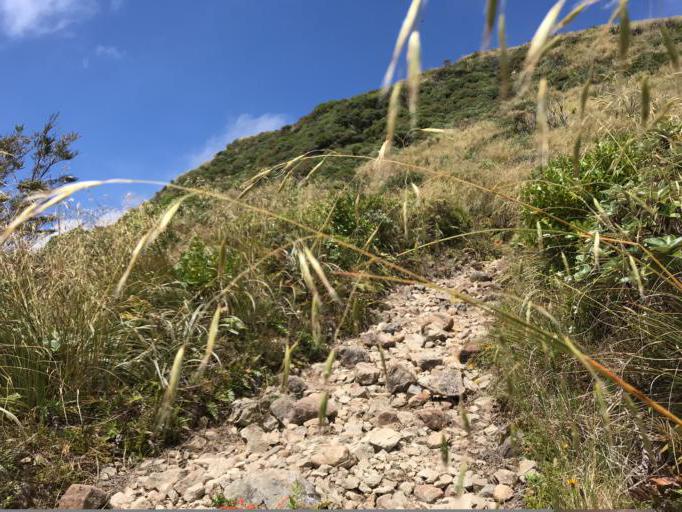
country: NZ
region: Wellington
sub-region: Kapiti Coast District
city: Otaki
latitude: -40.9103
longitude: 175.2607
